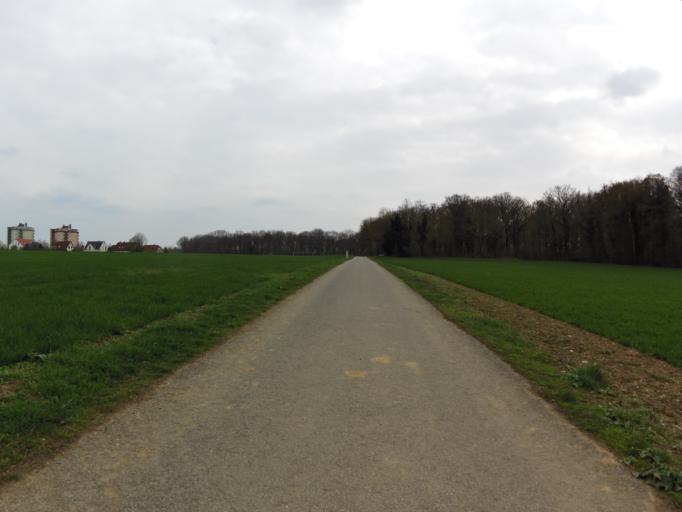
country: DE
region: Bavaria
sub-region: Regierungsbezirk Unterfranken
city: Rottendorf
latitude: 49.8016
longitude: 10.0183
